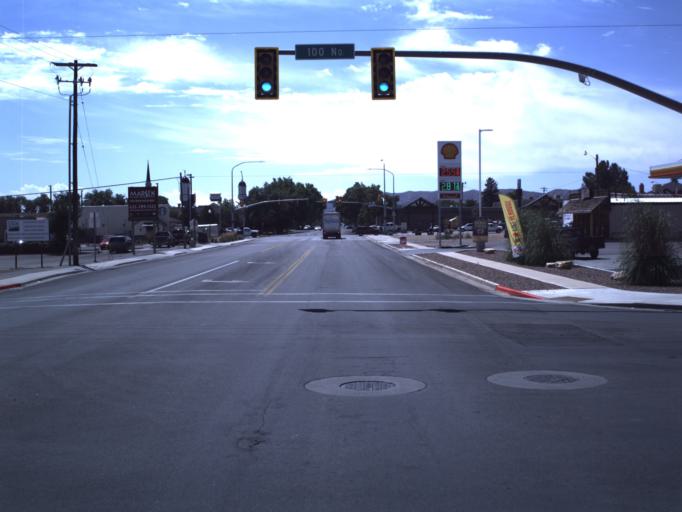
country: US
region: Utah
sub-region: Uintah County
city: Vernal
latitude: 40.4571
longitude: -109.5381
